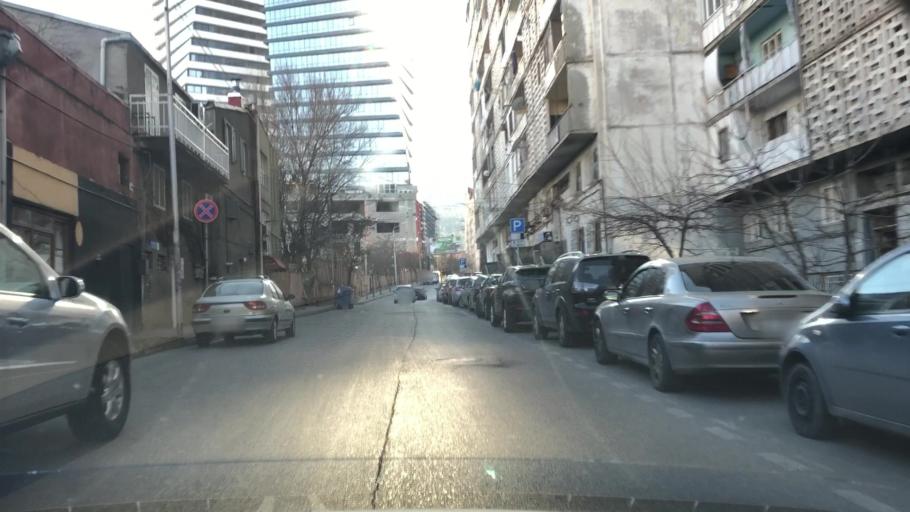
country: GE
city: Tsqnet'i
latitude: 41.7138
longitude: 44.7573
